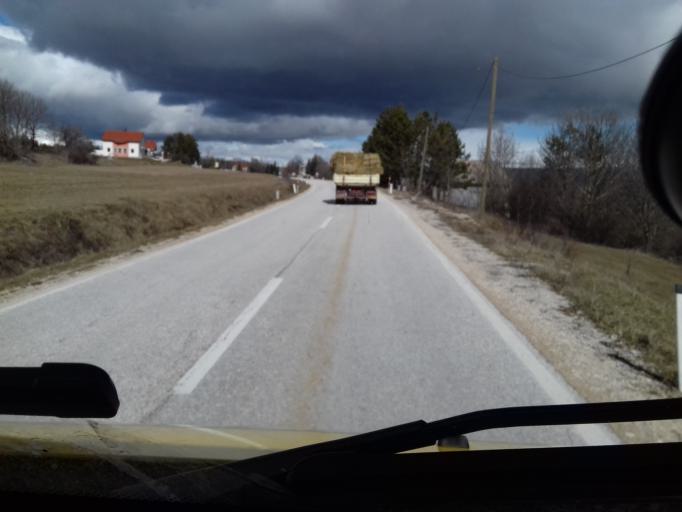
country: BA
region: Federation of Bosnia and Herzegovina
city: Dreznica
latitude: 43.5999
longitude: 17.2739
